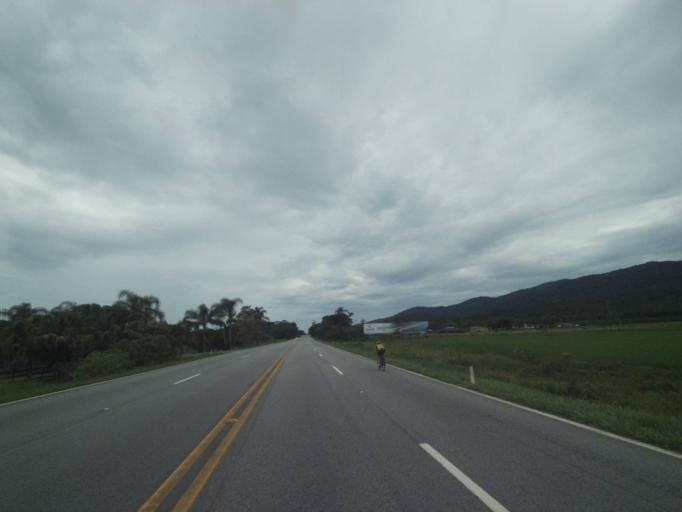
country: BR
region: Parana
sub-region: Pontal Do Parana
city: Pontal do Parana
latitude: -25.6301
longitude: -48.5954
